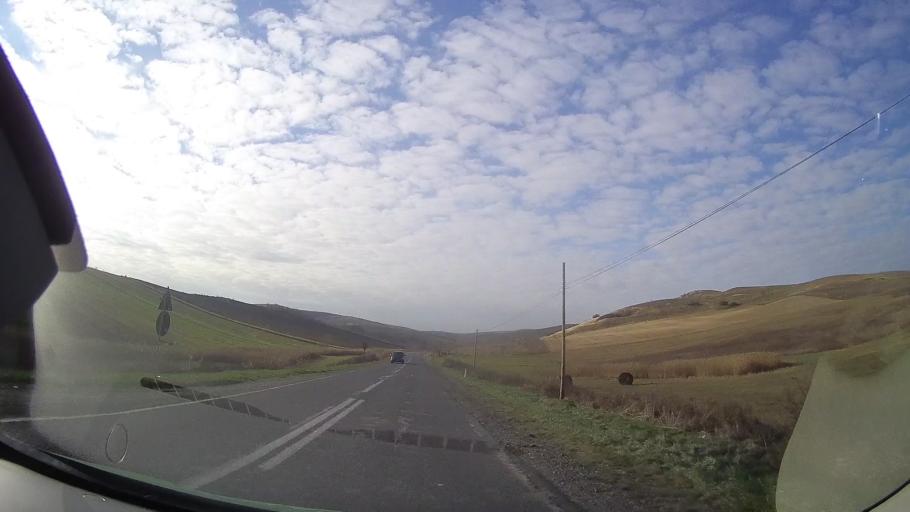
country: RO
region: Cluj
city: Jucu Herghelia
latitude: 46.8117
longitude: 23.8261
